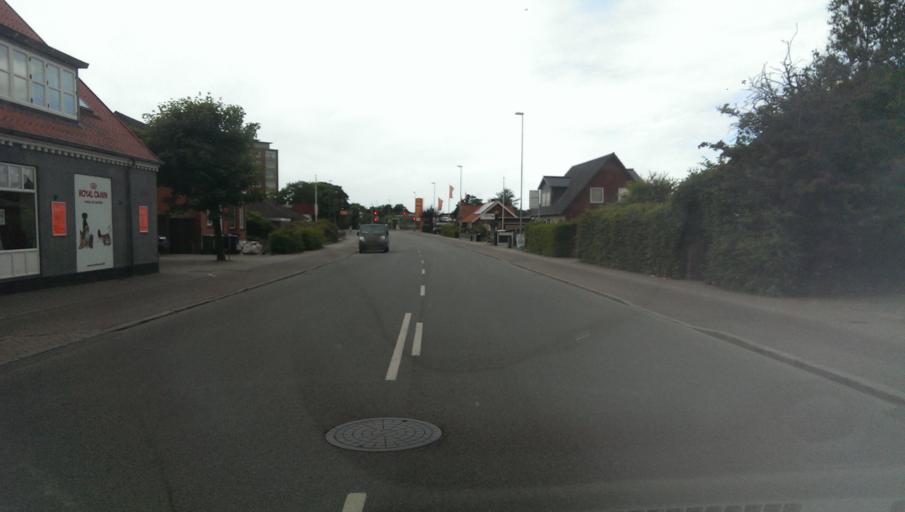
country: DK
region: South Denmark
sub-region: Esbjerg Kommune
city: Esbjerg
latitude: 55.4798
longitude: 8.4704
